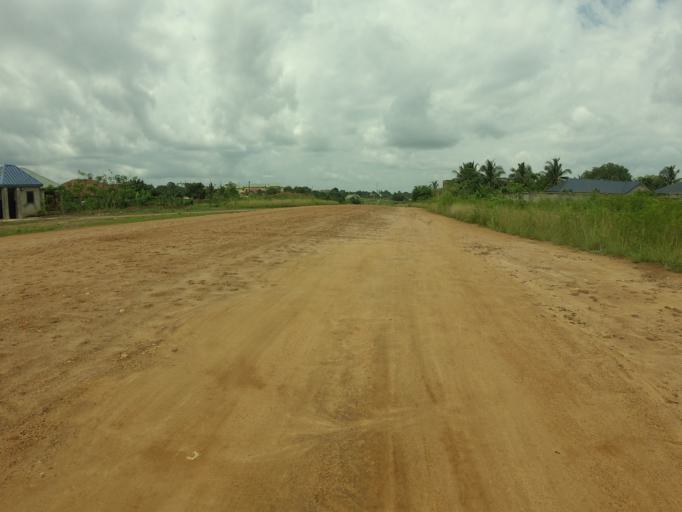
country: GH
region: Volta
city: Ho
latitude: 6.5838
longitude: 0.4603
